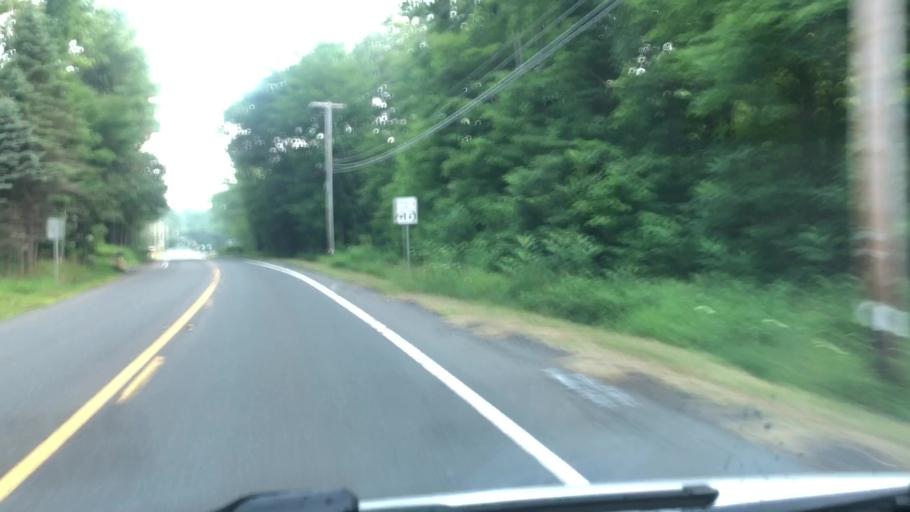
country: US
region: Massachusetts
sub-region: Hampshire County
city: Williamsburg
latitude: 42.3977
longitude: -72.7419
